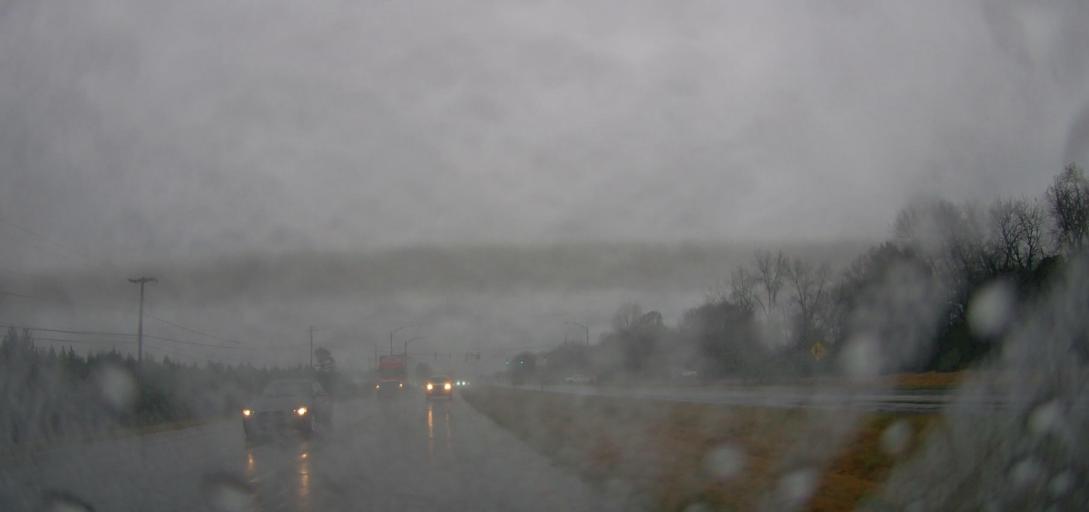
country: US
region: Alabama
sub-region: Elmore County
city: Millbrook
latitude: 32.3975
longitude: -86.3962
